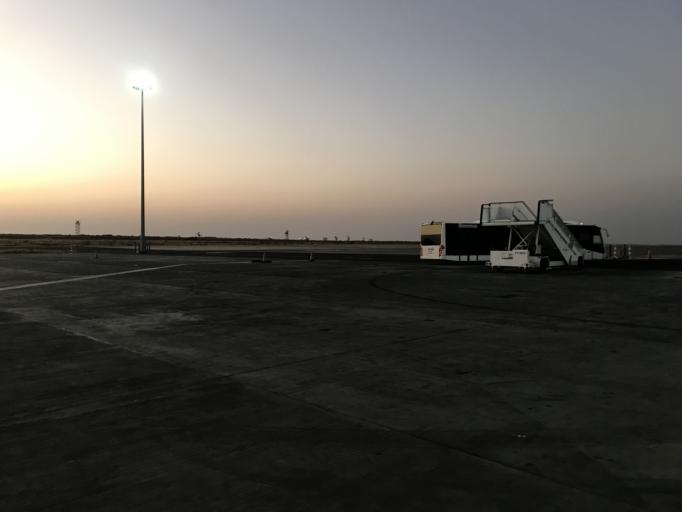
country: SN
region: Thies
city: Pout
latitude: 14.6677
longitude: -17.0683
